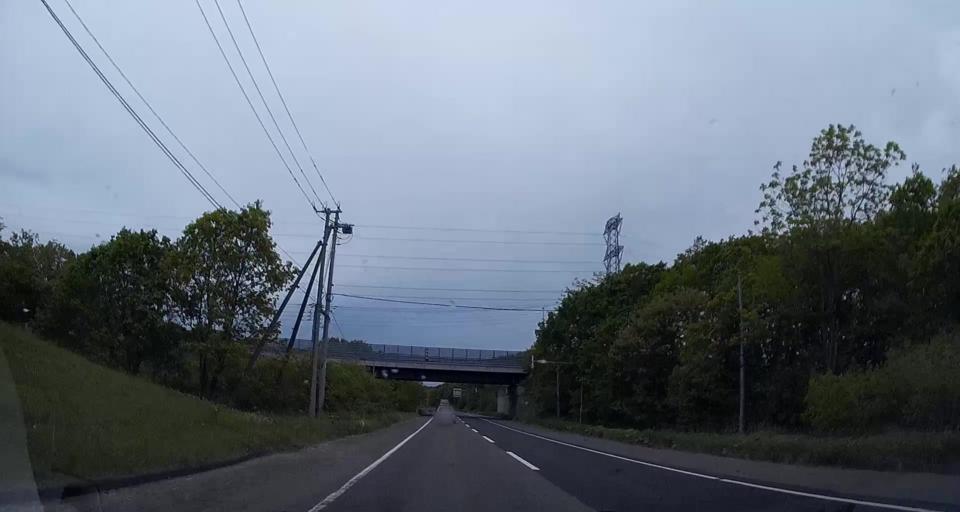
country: JP
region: Hokkaido
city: Chitose
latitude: 42.7104
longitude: 141.7477
